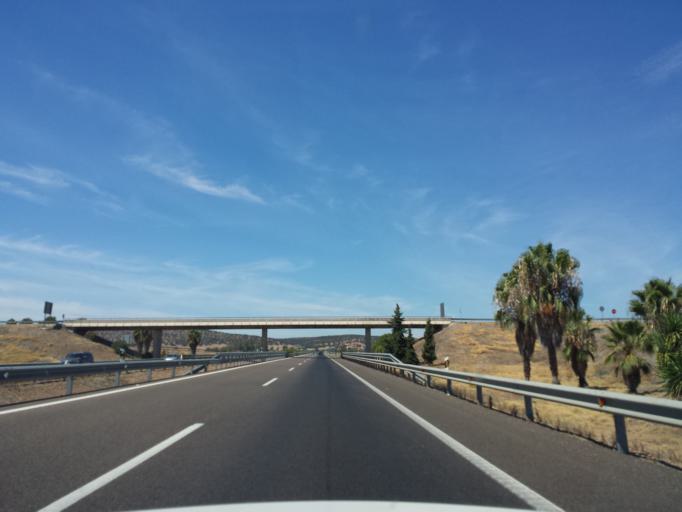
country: ES
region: Extremadura
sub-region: Provincia de Badajoz
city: San Pedro de Merida
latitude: 38.9900
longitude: -6.1203
